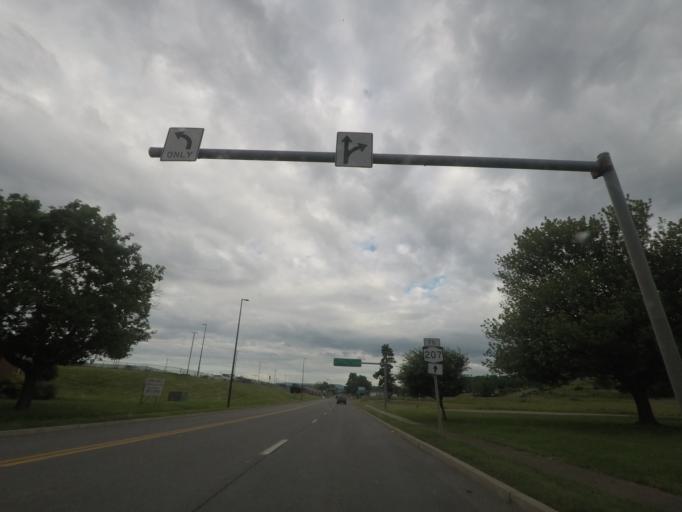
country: US
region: New York
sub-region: Orange County
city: Orange Lake
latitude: 41.4973
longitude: -74.1027
